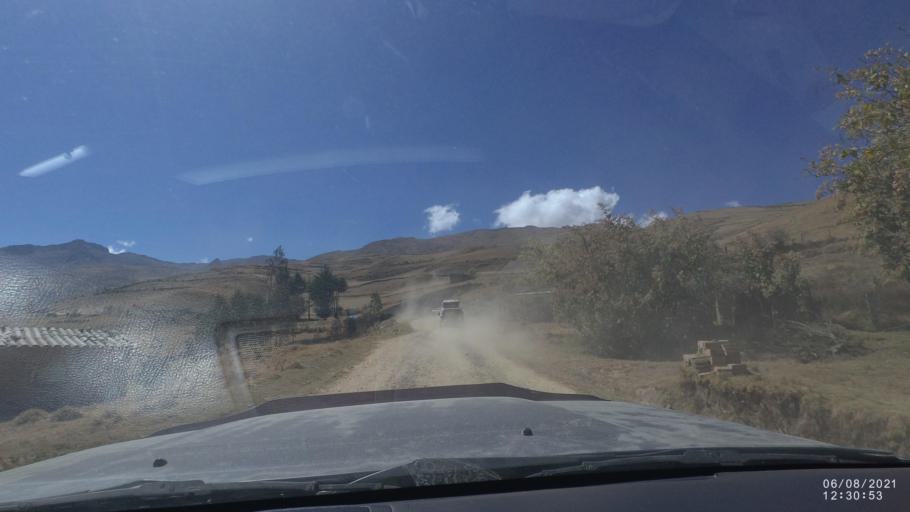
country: BO
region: Cochabamba
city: Colchani
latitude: -16.7879
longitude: -66.6485
